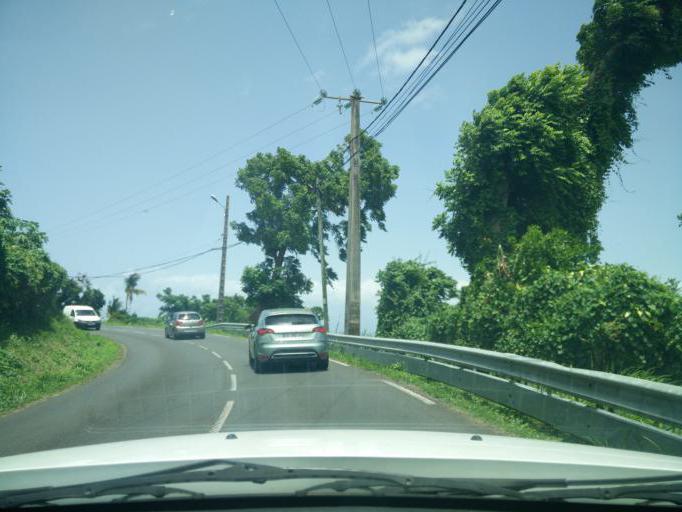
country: GP
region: Guadeloupe
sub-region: Guadeloupe
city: Trois-Rivieres
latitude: 15.9755
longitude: -61.6316
